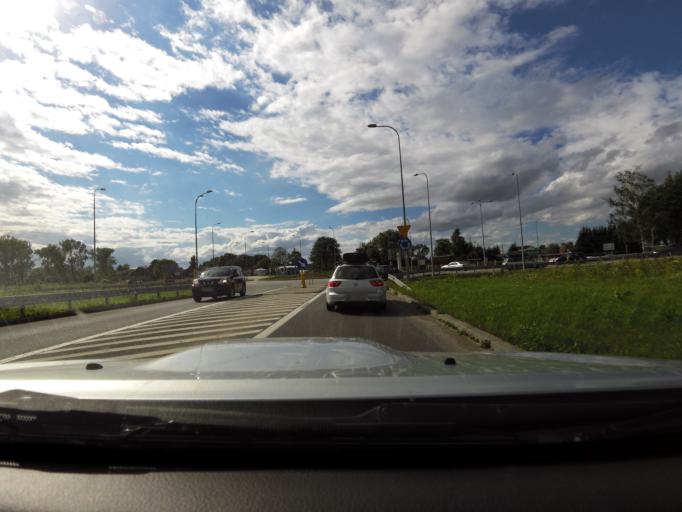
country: PL
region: Pomeranian Voivodeship
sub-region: Powiat gdanski
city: Cedry Wielkie
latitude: 54.2942
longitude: 18.8158
